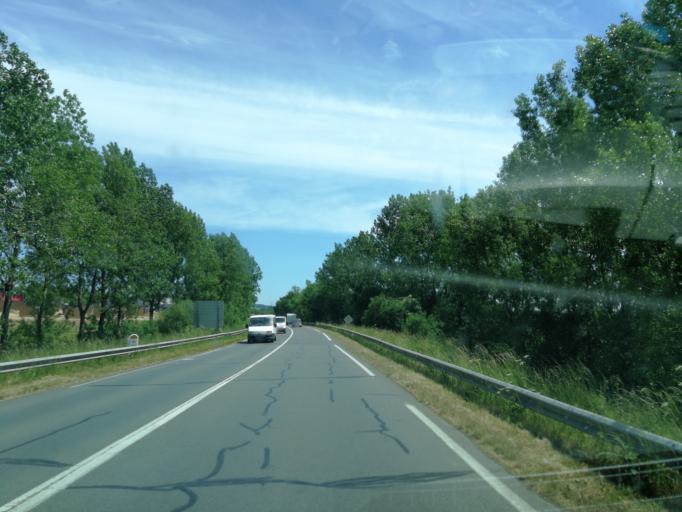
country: FR
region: Pays de la Loire
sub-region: Departement de la Vendee
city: La Chataigneraie
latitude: 46.6402
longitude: -0.7506
